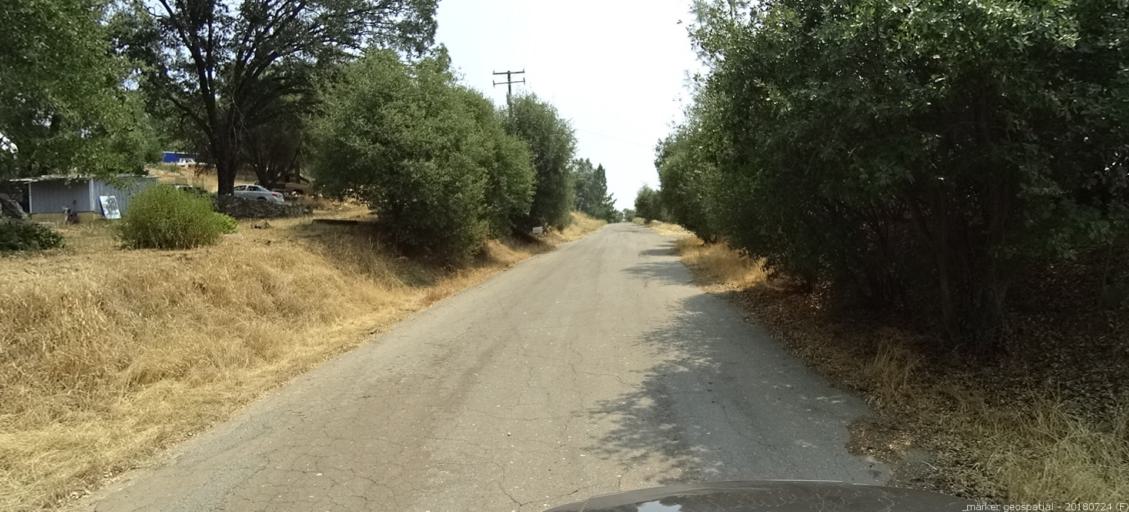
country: US
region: California
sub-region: Madera County
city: Oakhurst
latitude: 37.2453
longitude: -119.5577
